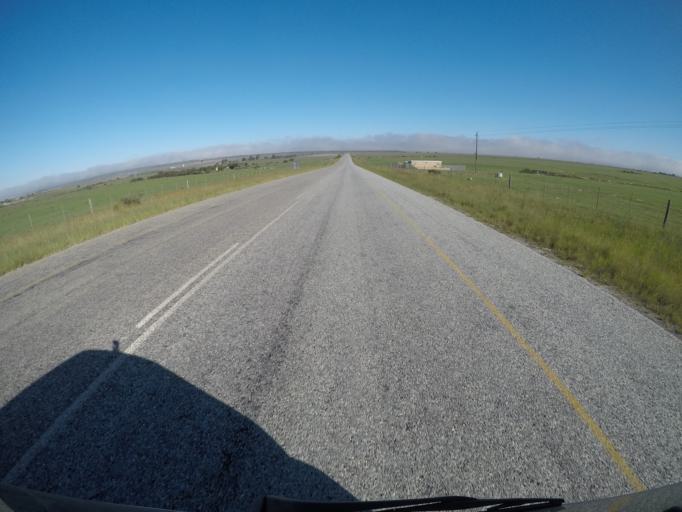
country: ZA
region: Western Cape
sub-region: Eden District Municipality
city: Mossel Bay
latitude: -34.1692
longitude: 22.0131
